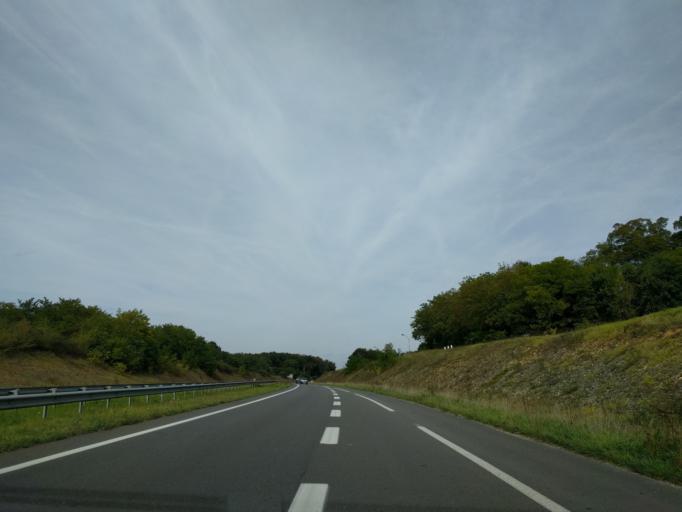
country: FR
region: Centre
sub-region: Departement du Cher
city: Bourges
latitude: 47.0608
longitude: 2.4312
